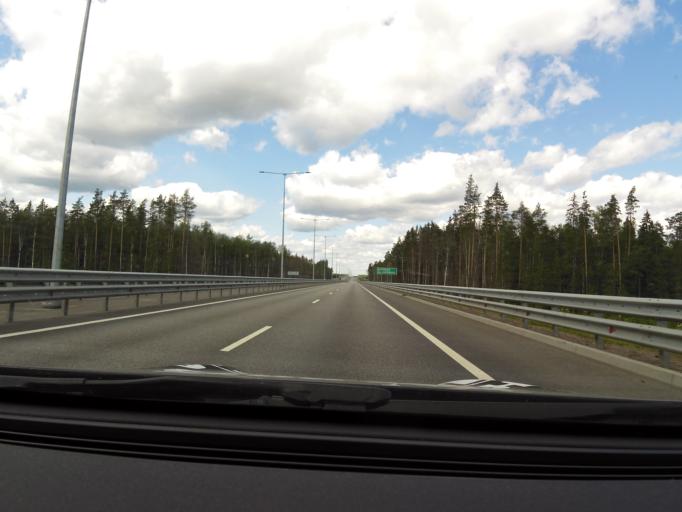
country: RU
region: Tverskaya
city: Vyshniy Volochek
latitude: 57.4293
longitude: 34.4756
